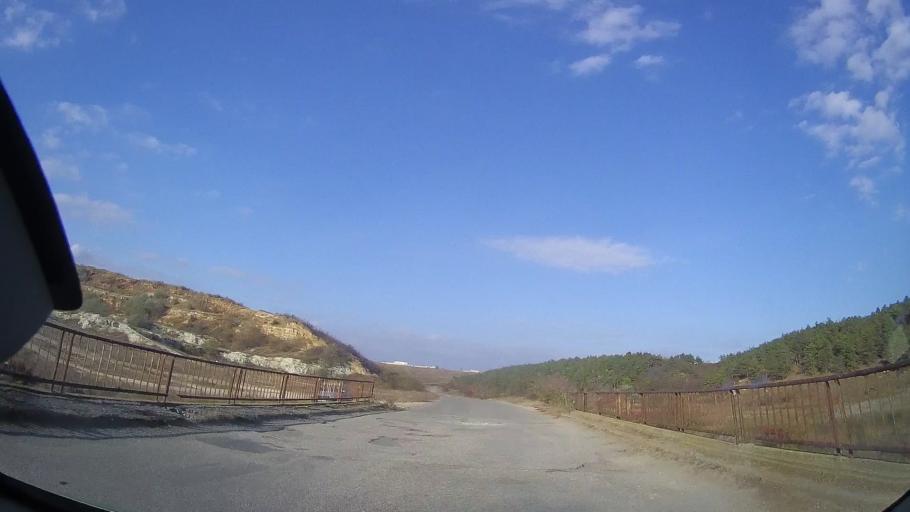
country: RO
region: Constanta
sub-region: Comuna Limanu
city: Limanu
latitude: 43.8140
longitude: 28.5172
